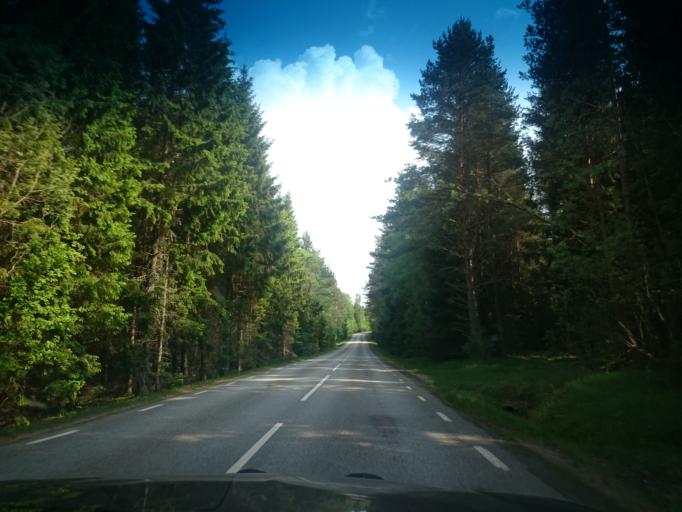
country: SE
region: Joenkoeping
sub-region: Vetlanda Kommun
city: Vetlanda
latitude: 57.3322
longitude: 15.0825
